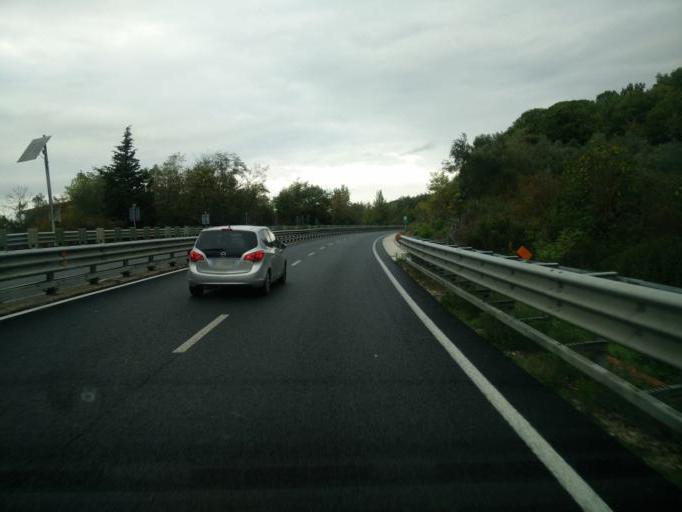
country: IT
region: Tuscany
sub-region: Province of Florence
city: Sambuca
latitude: 43.5465
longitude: 11.2117
